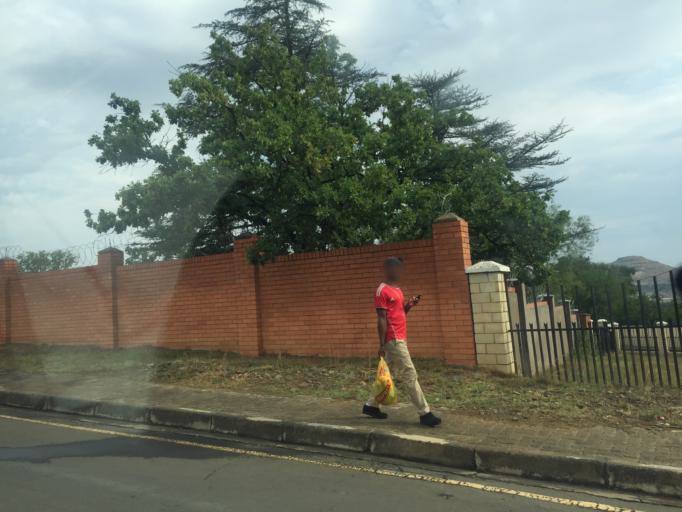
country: LS
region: Maseru
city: Maseru
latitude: -29.3068
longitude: 27.4746
